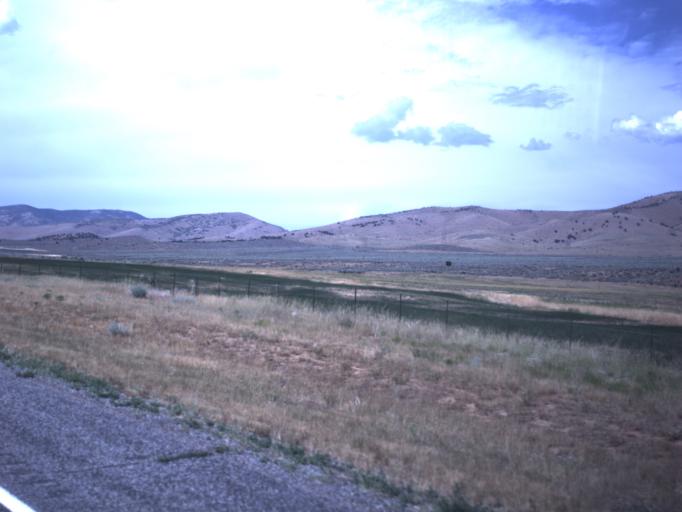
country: US
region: Utah
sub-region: Sanpete County
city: Fountain Green
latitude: 39.6419
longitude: -111.6361
